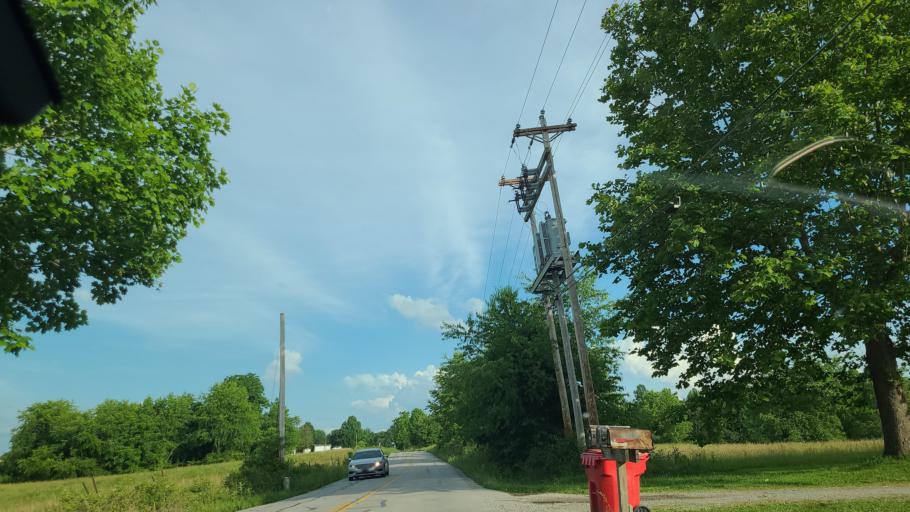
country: US
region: Kentucky
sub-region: Whitley County
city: Corbin
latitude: 36.8993
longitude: -84.2348
